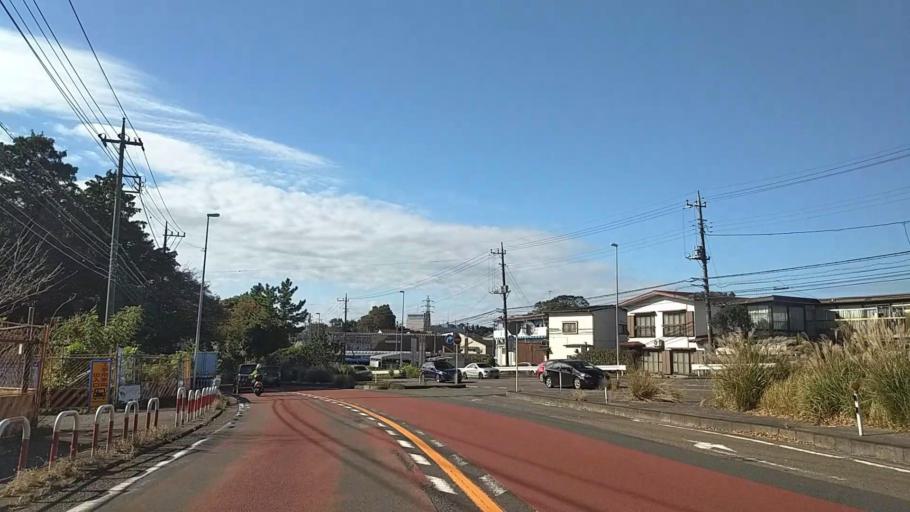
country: JP
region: Kanagawa
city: Fujisawa
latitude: 35.3866
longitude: 139.5178
